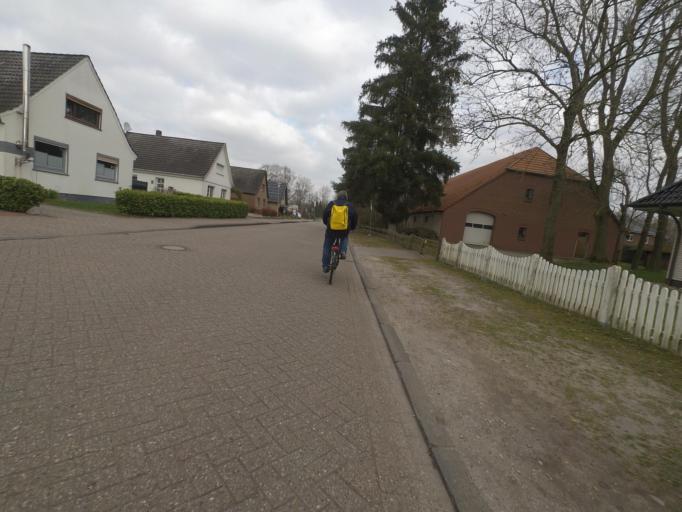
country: DE
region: Lower Saxony
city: Oldenburg
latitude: 53.1005
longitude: 8.2510
